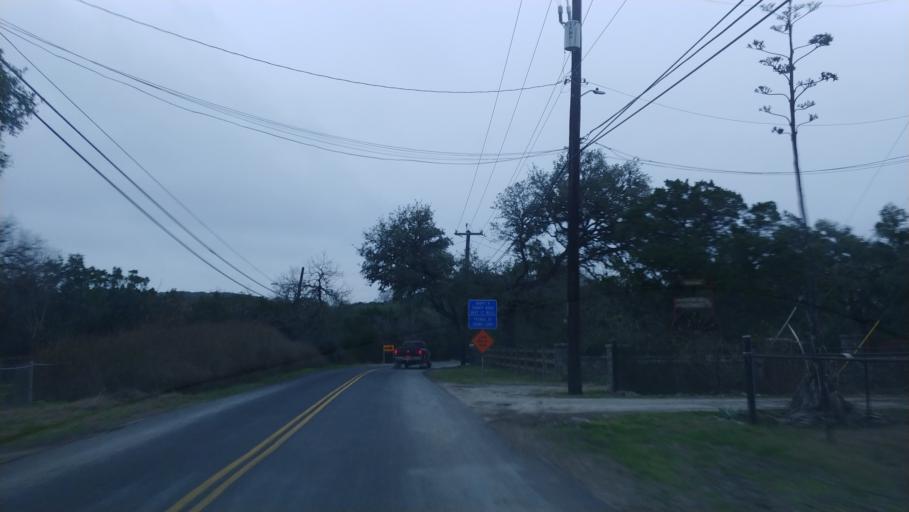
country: US
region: Texas
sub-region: Bexar County
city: Helotes
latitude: 29.6090
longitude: -98.6847
